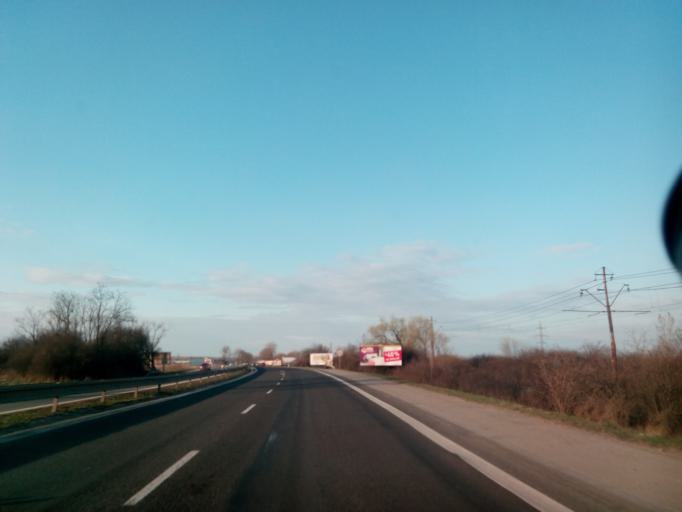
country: SK
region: Kosicky
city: Kosice
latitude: 48.6469
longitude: 21.2032
